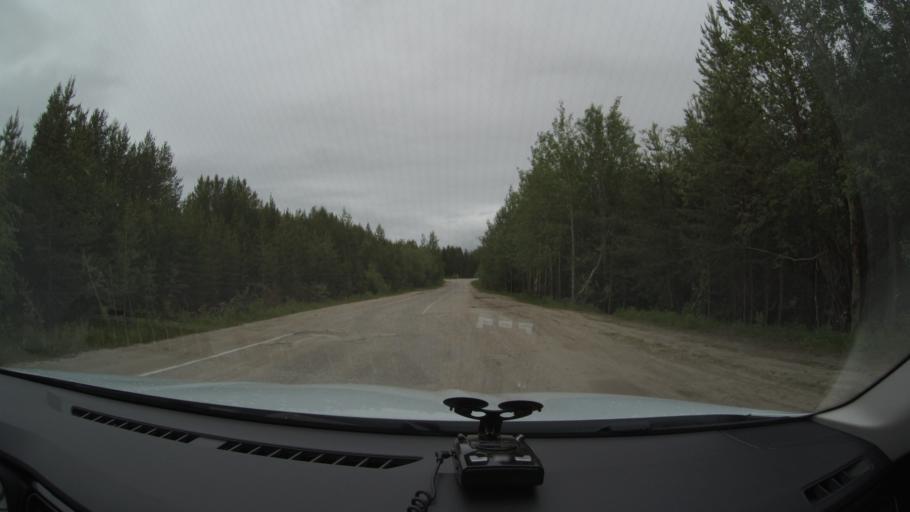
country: RU
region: Komi Republic
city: Kozhva
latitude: 65.1090
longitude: 56.9972
